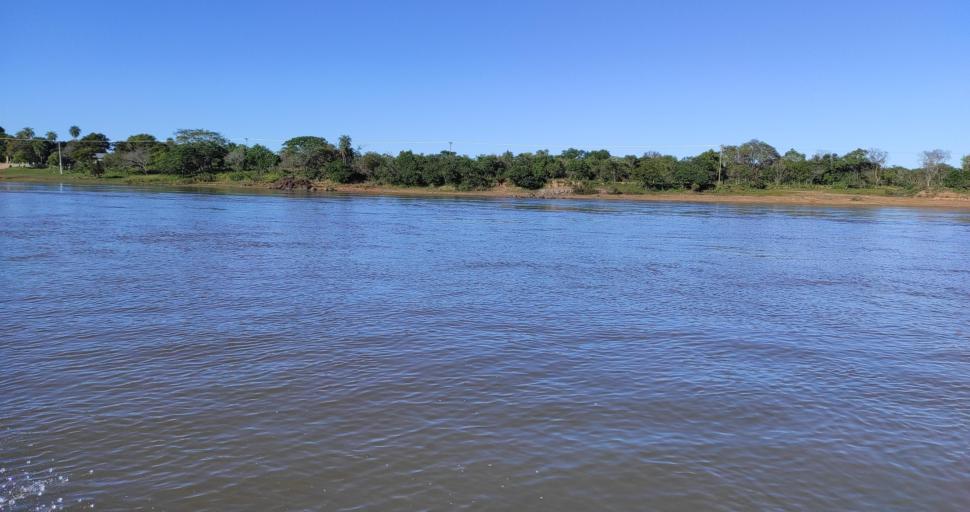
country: AR
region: Corrientes
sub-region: Departamento de Itati
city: Itati
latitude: -27.2634
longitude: -58.2592
